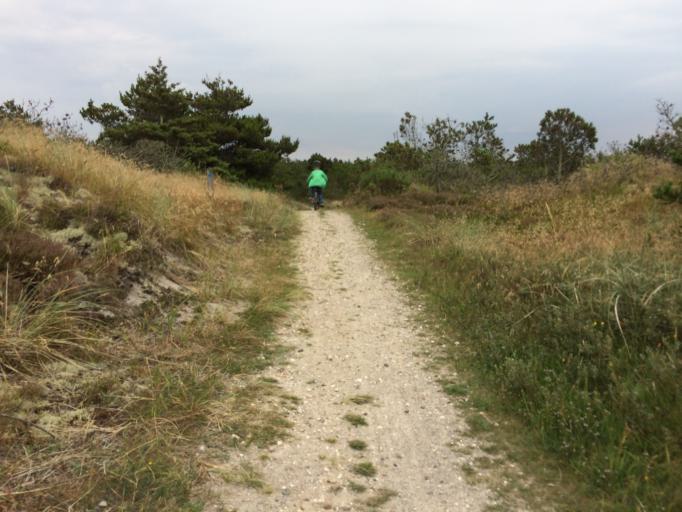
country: DK
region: Central Jutland
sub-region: Holstebro Kommune
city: Ulfborg
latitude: 56.2865
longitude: 8.1361
